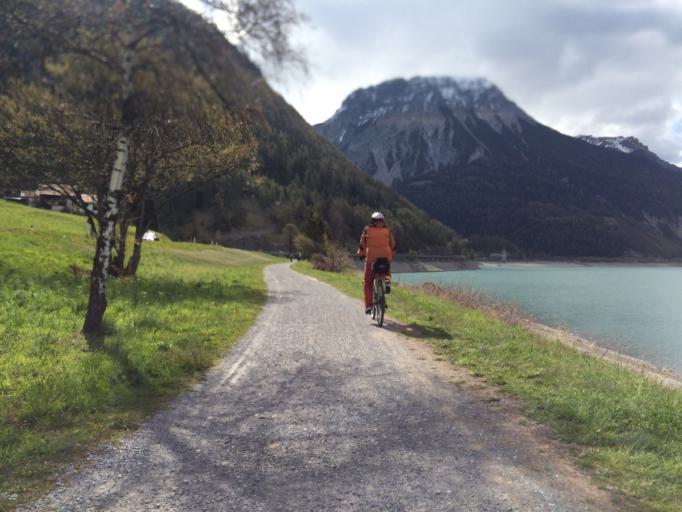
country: IT
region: Trentino-Alto Adige
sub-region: Bolzano
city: Curon Venosta
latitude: 46.8191
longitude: 10.5256
